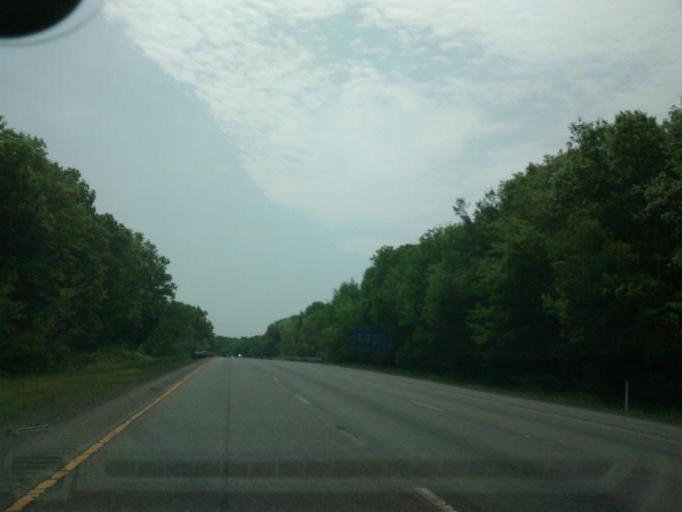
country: US
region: Massachusetts
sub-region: Worcester County
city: Milford
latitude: 42.1819
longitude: -71.5299
